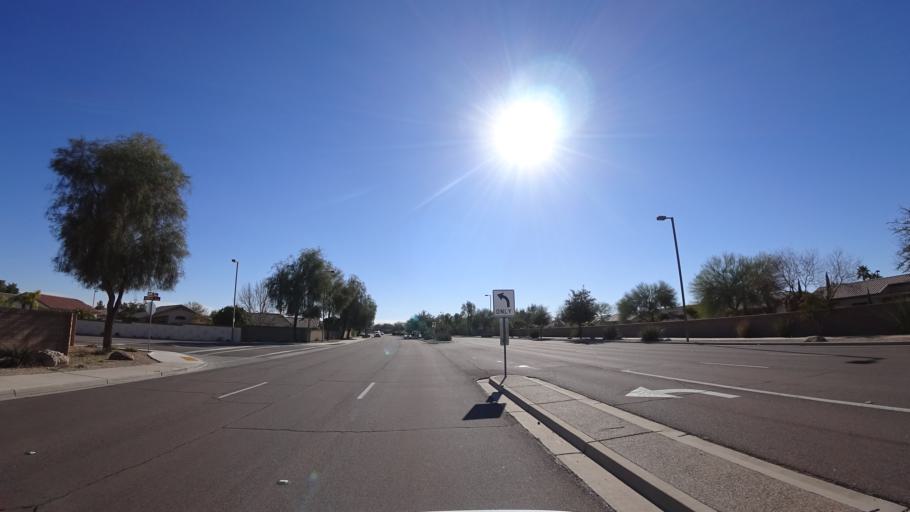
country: US
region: Arizona
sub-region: Maricopa County
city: Sun City West
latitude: 33.6423
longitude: -112.3934
